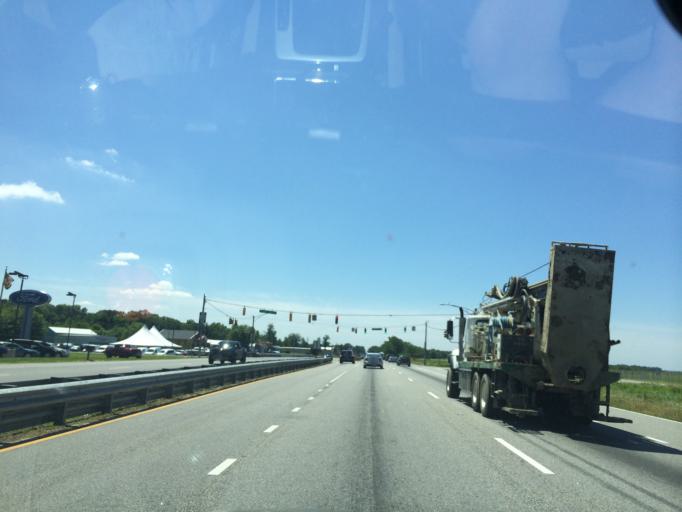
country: US
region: Maryland
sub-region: Talbot County
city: Easton
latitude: 38.8137
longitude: -76.0601
